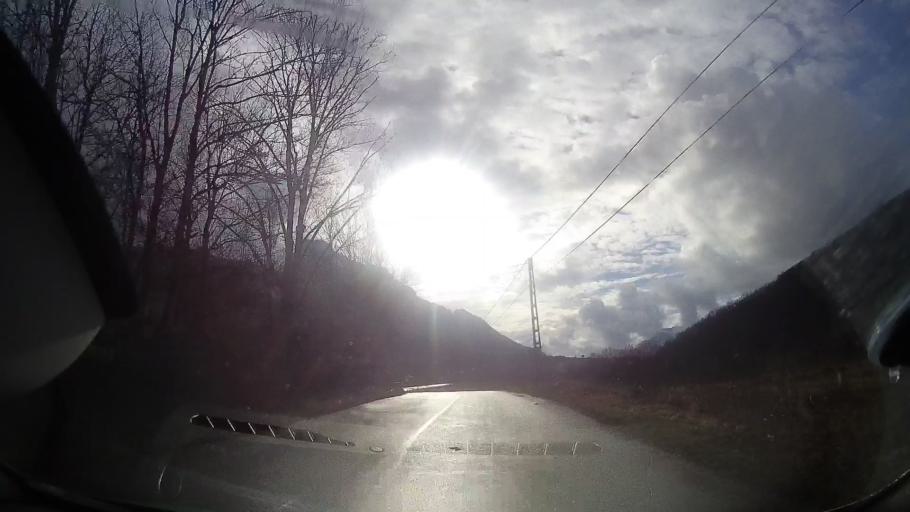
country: RO
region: Alba
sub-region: Comuna Rimetea
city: Rimetea
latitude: 46.4740
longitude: 23.5846
